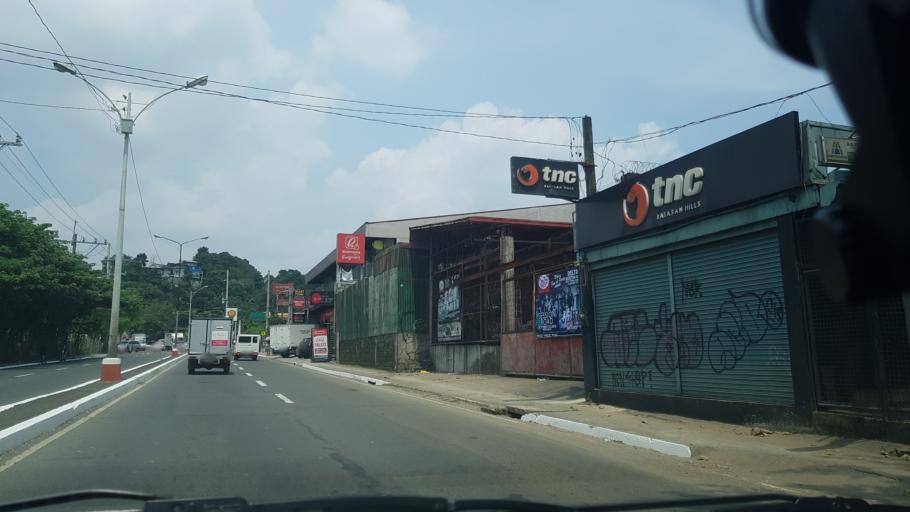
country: PH
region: Calabarzon
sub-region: Province of Rizal
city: San Mateo
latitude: 14.6835
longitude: 121.1057
